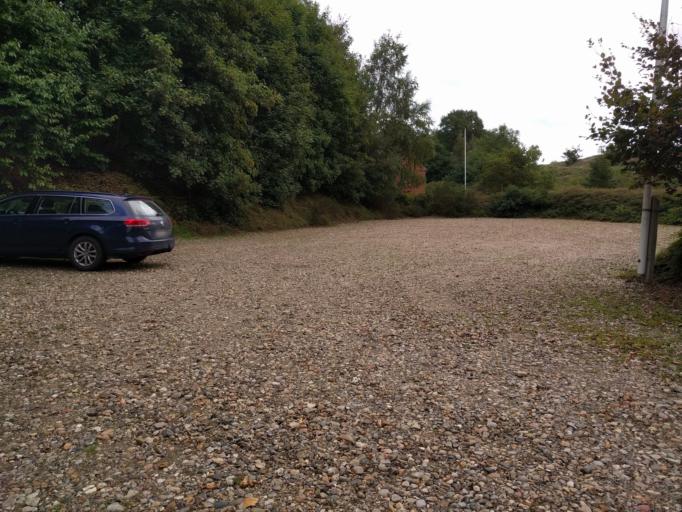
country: DK
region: Central Jutland
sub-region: Viborg Kommune
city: Stoholm
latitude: 56.4382
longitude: 9.1309
